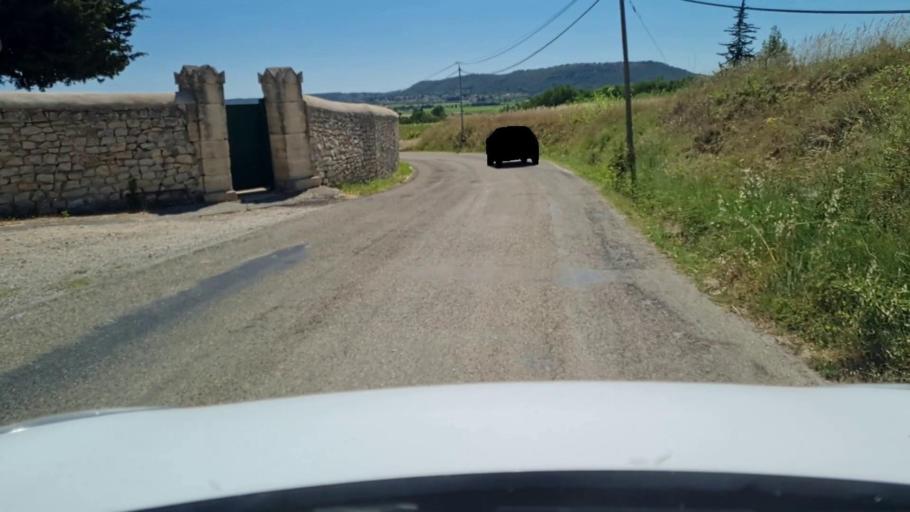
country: FR
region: Languedoc-Roussillon
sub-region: Departement du Gard
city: Calvisson
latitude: 43.8104
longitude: 4.1888
